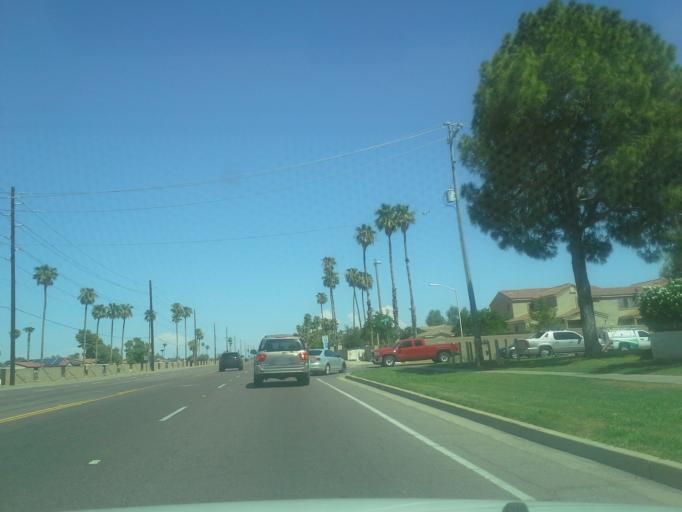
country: US
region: Arizona
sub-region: Maricopa County
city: Litchfield Park
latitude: 33.5368
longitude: -112.3501
